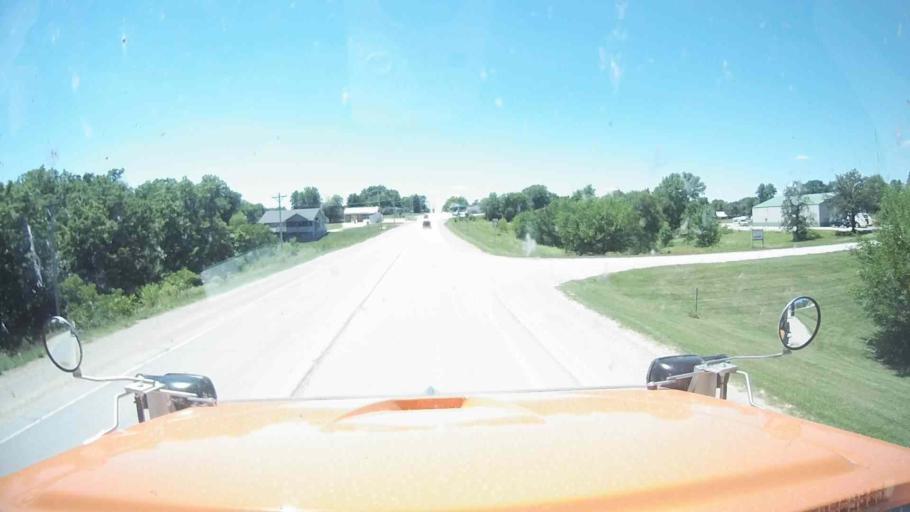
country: US
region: Iowa
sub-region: Taylor County
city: Bedford
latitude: 40.6768
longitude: -94.7180
